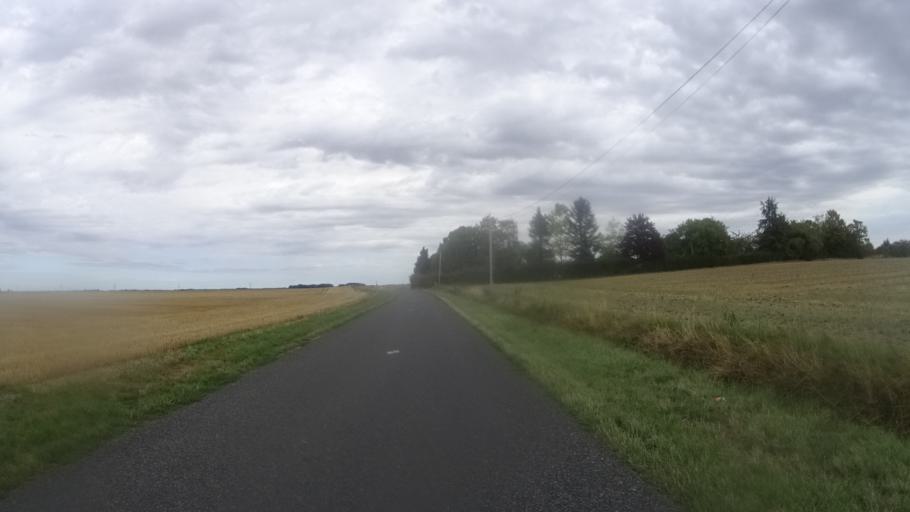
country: FR
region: Centre
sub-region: Departement du Loiret
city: Boynes
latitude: 48.0740
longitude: 2.3006
